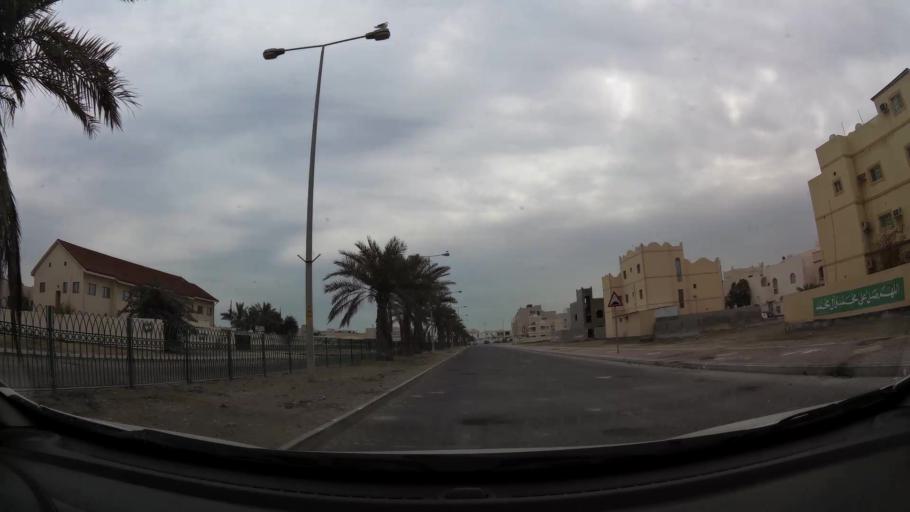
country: BH
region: Northern
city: Sitrah
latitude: 26.1585
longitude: 50.6187
